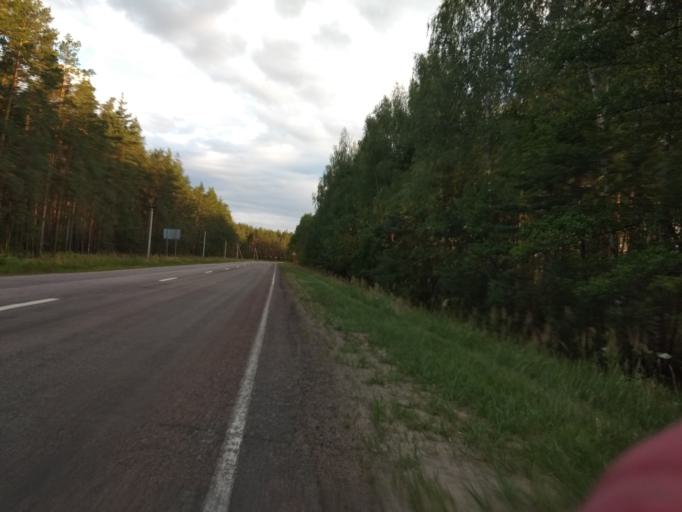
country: RU
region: Moskovskaya
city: Misheronskiy
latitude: 55.6297
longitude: 39.7418
